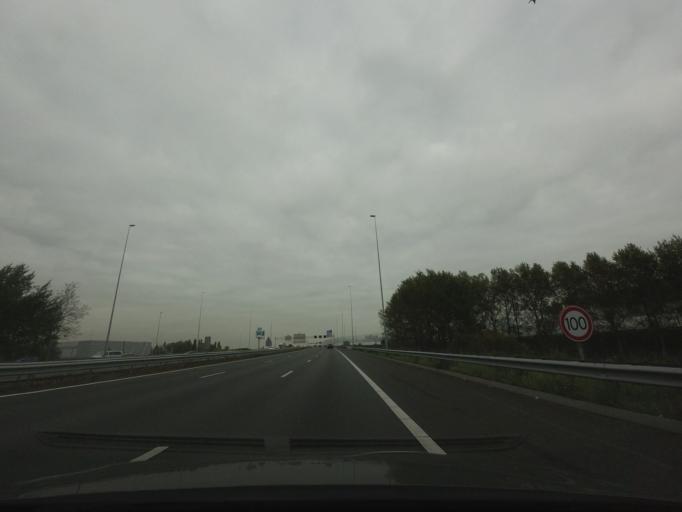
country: NL
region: North Holland
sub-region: Gemeente Diemen
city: Diemen
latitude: 52.3515
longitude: 4.9632
